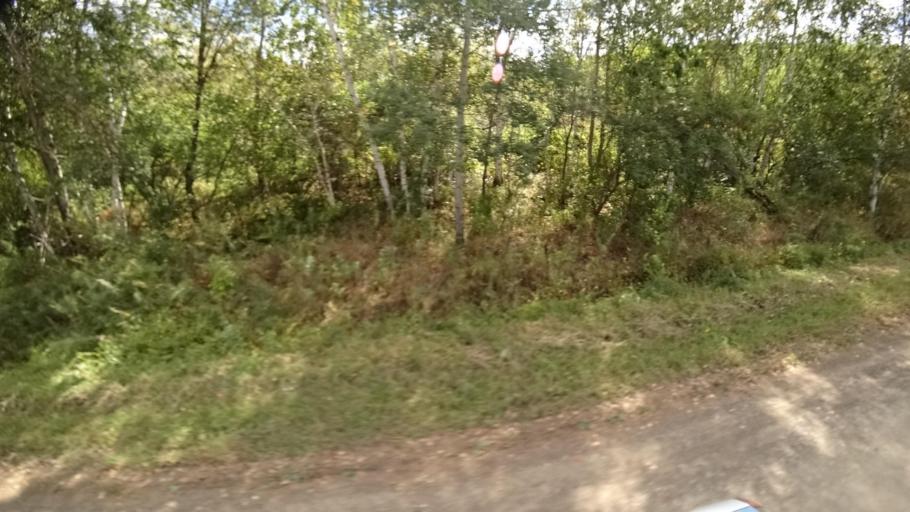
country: RU
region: Primorskiy
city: Yakovlevka
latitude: 44.7020
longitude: 133.6471
